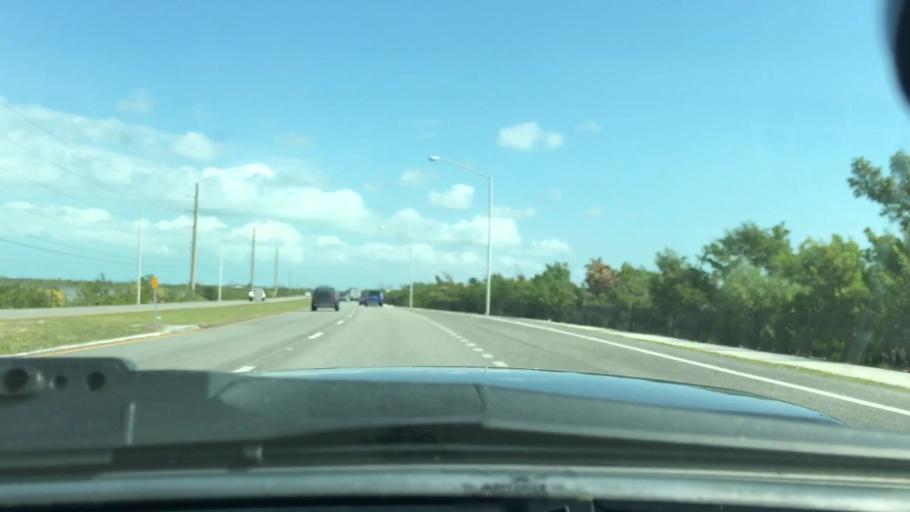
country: US
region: Florida
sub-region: Monroe County
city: Stock Island
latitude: 24.5800
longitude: -81.7066
